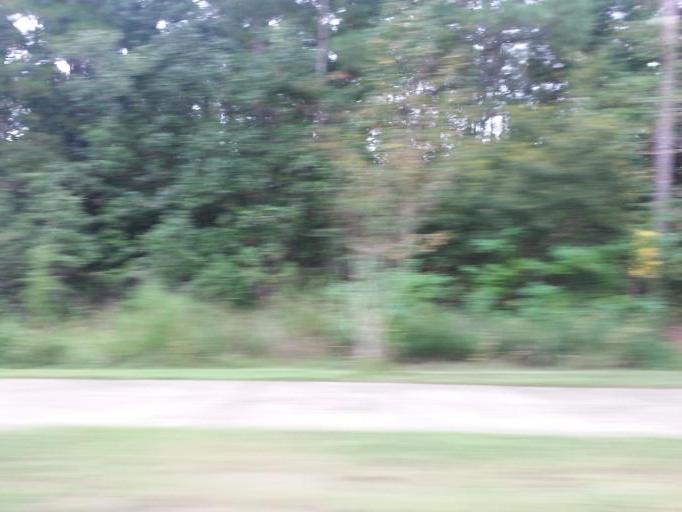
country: US
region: Alabama
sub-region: Baldwin County
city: Point Clear
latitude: 30.4543
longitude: -87.9152
